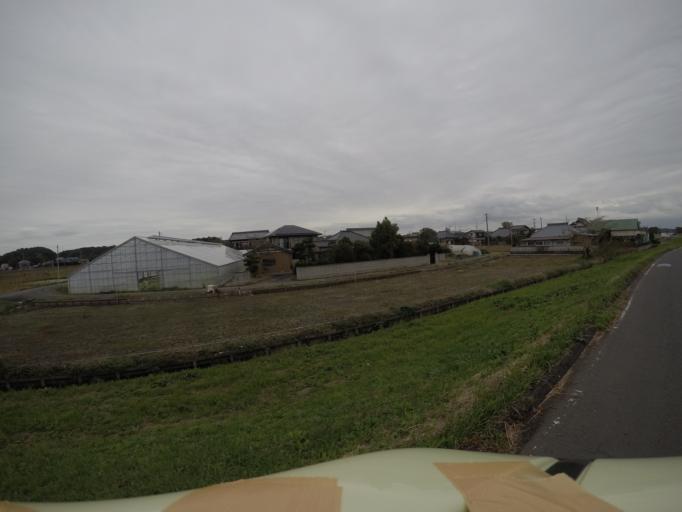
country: JP
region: Ibaraki
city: Ami
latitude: 36.0683
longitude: 140.2511
